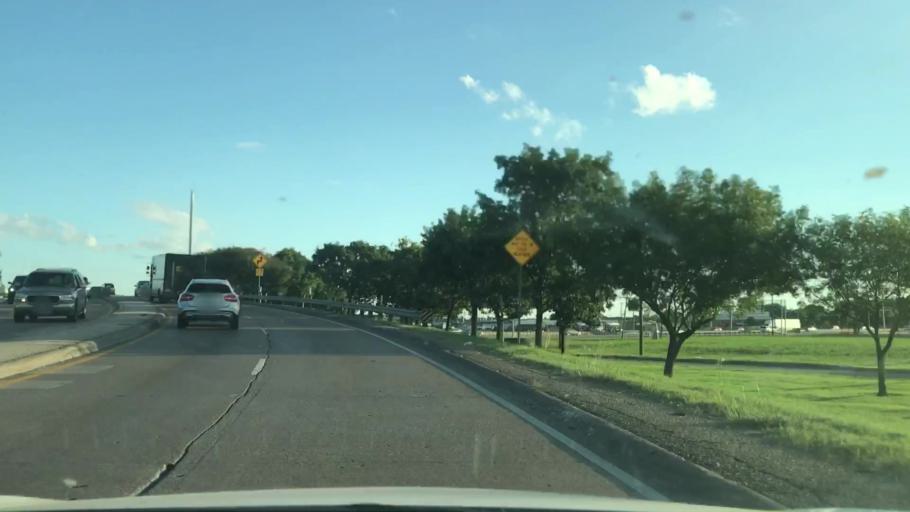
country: US
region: Texas
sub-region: Dallas County
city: Mesquite
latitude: 32.8051
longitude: -96.6686
